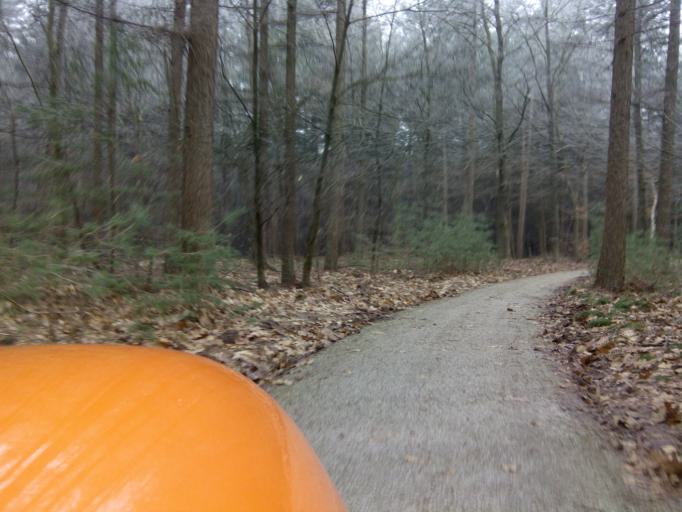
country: NL
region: Gelderland
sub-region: Gemeente Putten
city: Putten
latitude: 52.2585
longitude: 5.6372
